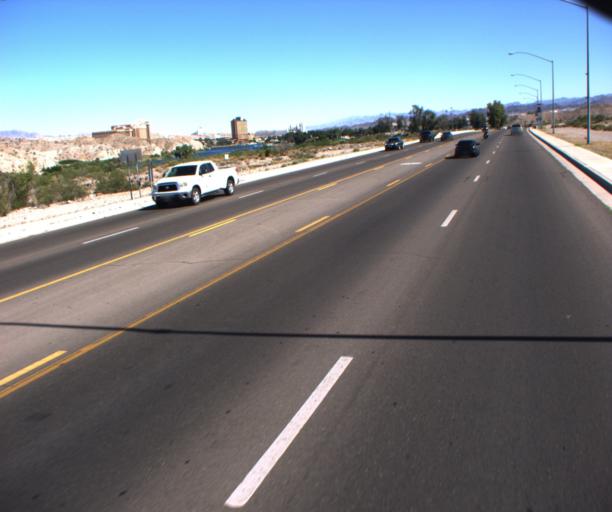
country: US
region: Arizona
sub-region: Mohave County
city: Bullhead City
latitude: 35.1328
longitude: -114.5727
